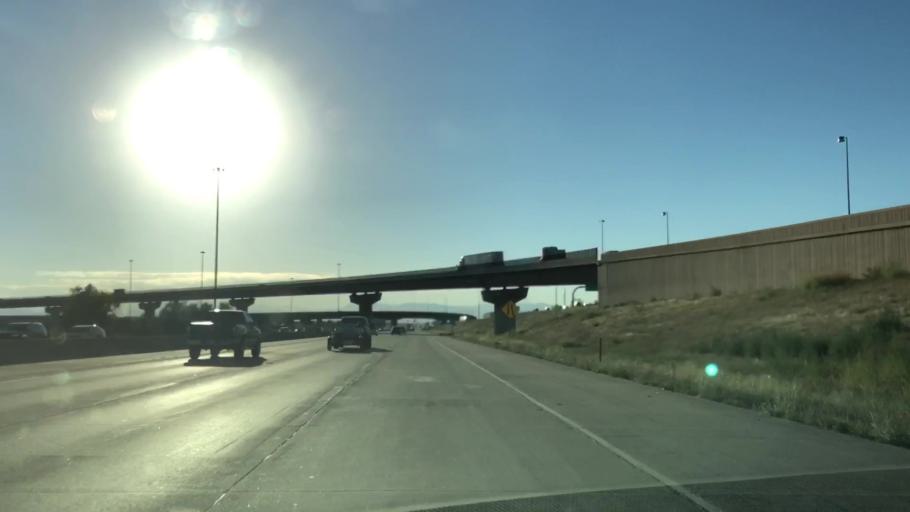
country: US
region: Colorado
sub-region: Adams County
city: Aurora
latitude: 39.7730
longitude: -104.8226
